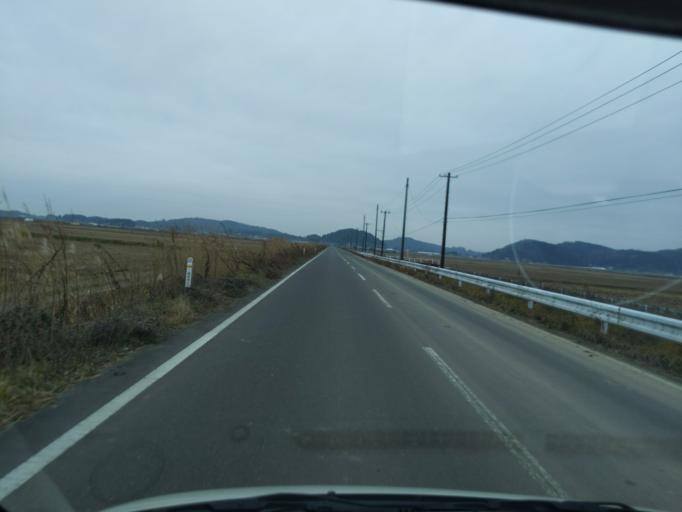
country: JP
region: Iwate
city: Ichinoseki
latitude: 38.7463
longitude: 141.2437
